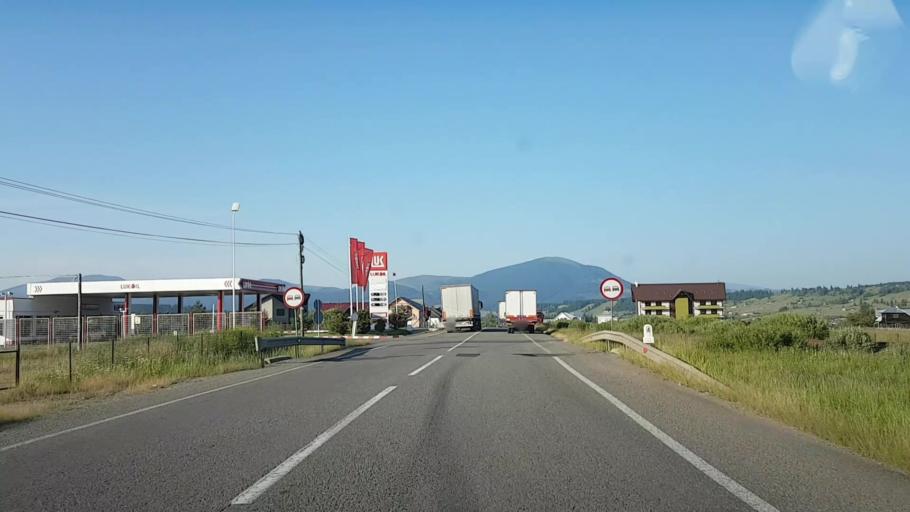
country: RO
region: Suceava
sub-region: Comuna Poiana Stampei
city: Poiana Stampei
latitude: 47.3264
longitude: 25.1429
